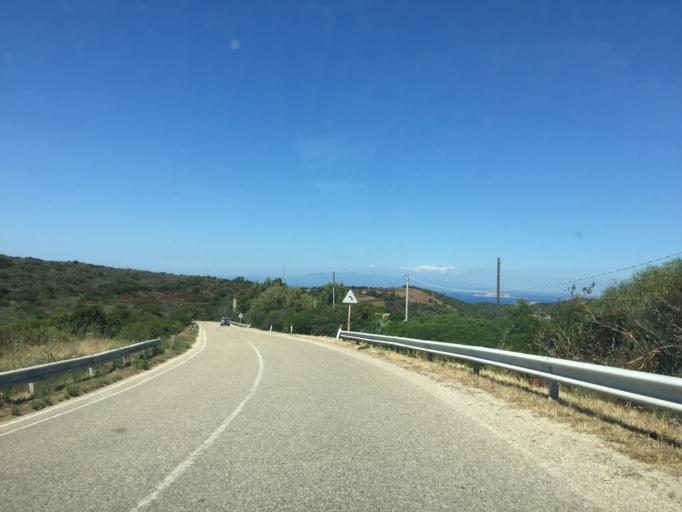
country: IT
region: Sardinia
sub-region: Provincia di Olbia-Tempio
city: Aglientu
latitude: 41.0961
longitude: 9.1003
